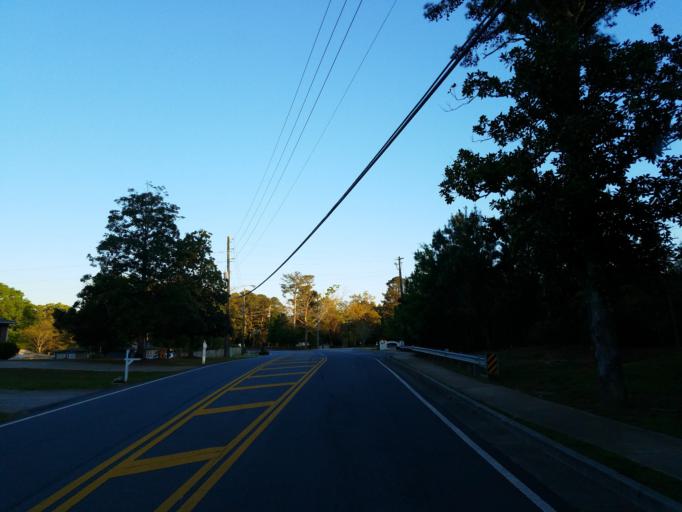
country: US
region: Georgia
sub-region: Cobb County
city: Powder Springs
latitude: 33.8866
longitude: -84.6190
